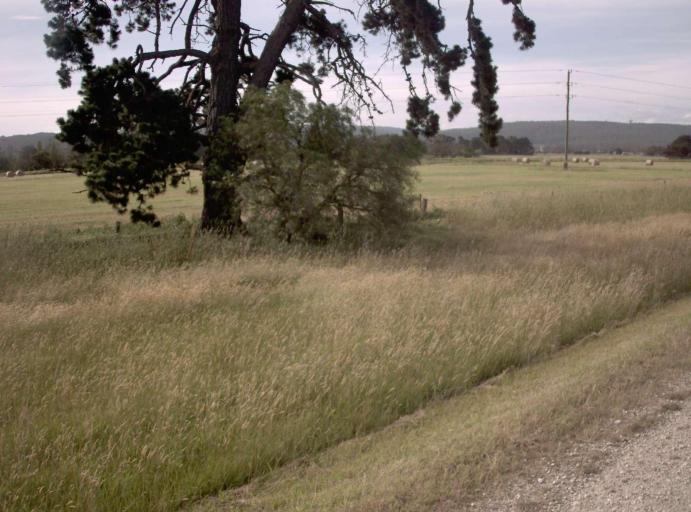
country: AU
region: Victoria
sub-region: Latrobe
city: Traralgon
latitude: -38.1038
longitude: 146.5932
